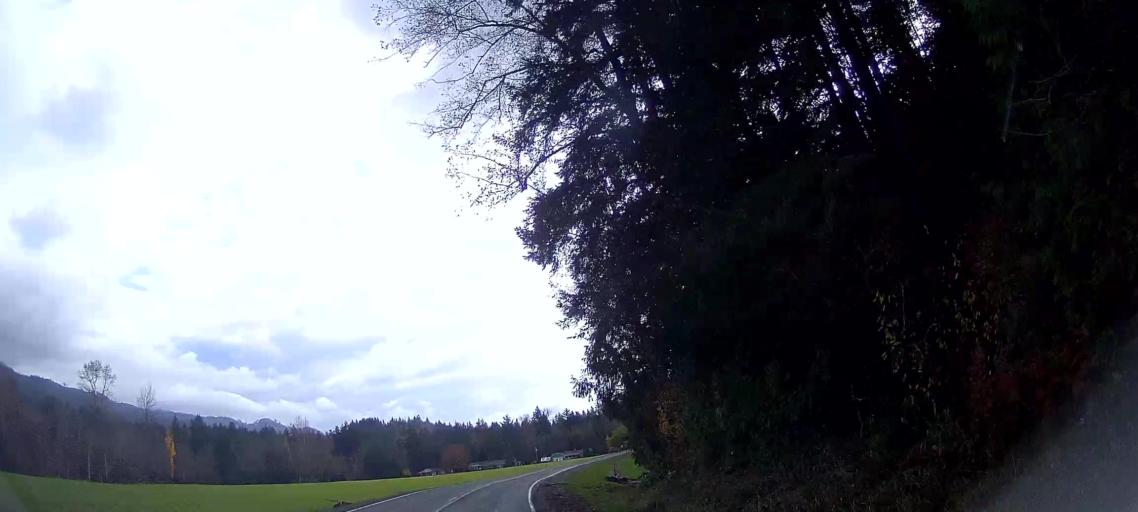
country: US
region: Washington
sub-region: Skagit County
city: Big Lake
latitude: 48.4167
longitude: -122.2071
